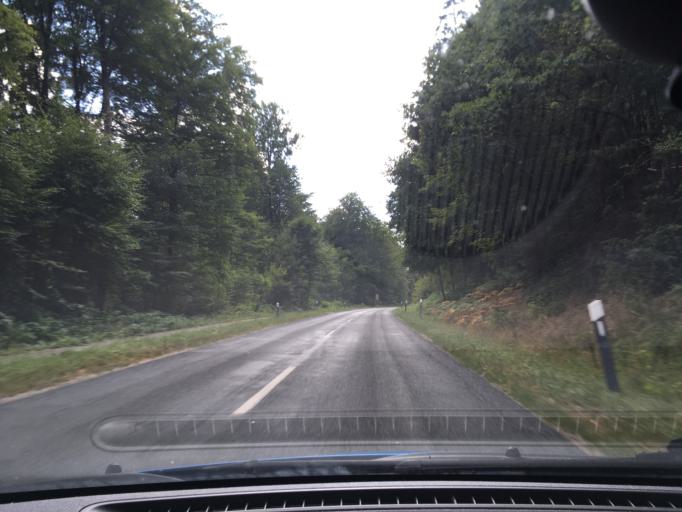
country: DE
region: Lower Saxony
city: Rehlingen
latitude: 53.0952
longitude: 10.2103
